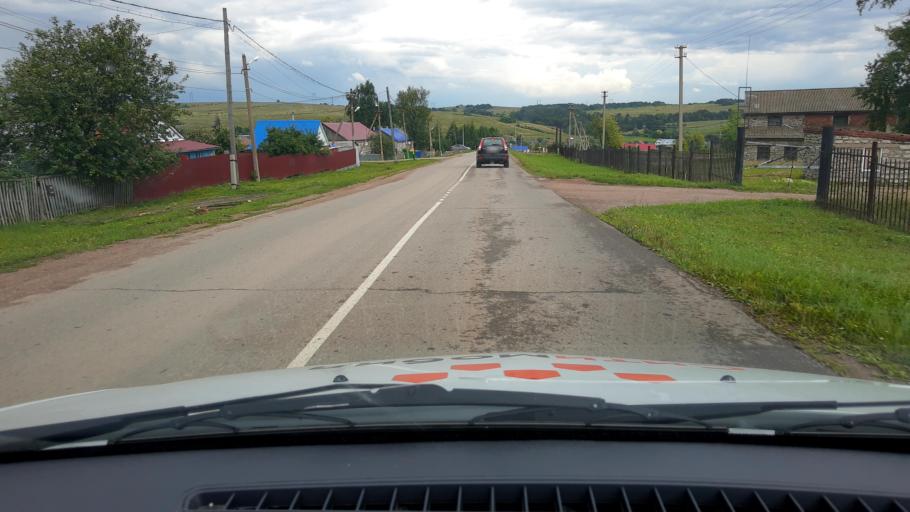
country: RU
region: Bashkortostan
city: Iglino
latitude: 54.9044
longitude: 56.1949
